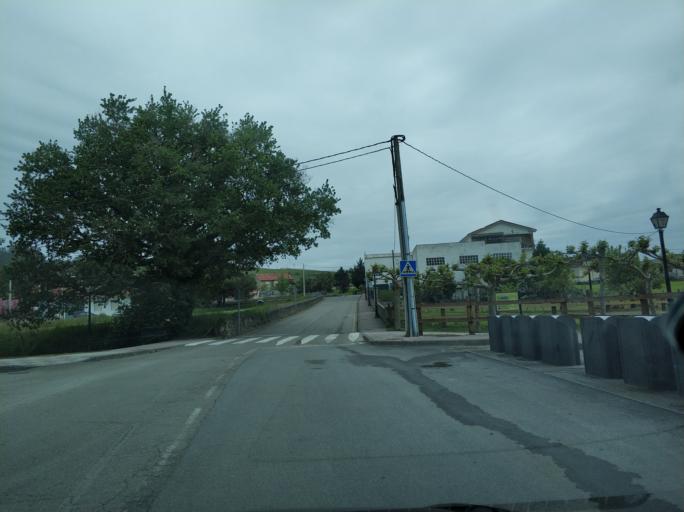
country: ES
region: Cantabria
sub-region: Provincia de Cantabria
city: Santa Maria de Cayon
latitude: 43.3224
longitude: -3.8569
